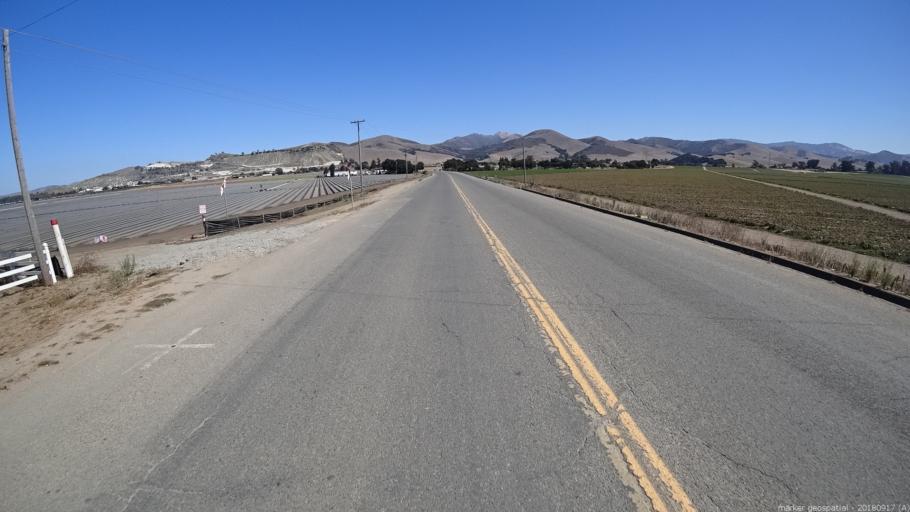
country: US
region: California
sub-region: Monterey County
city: Salinas
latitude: 36.7318
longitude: -121.6111
